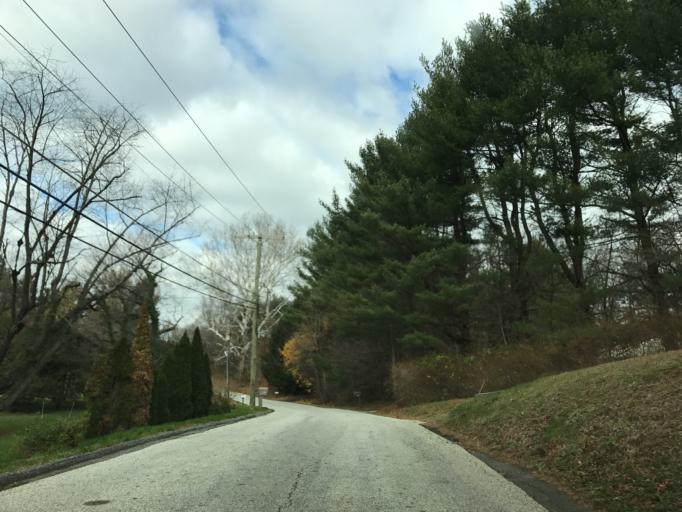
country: US
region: Maryland
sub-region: Baltimore County
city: Perry Hall
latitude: 39.4781
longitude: -76.5158
